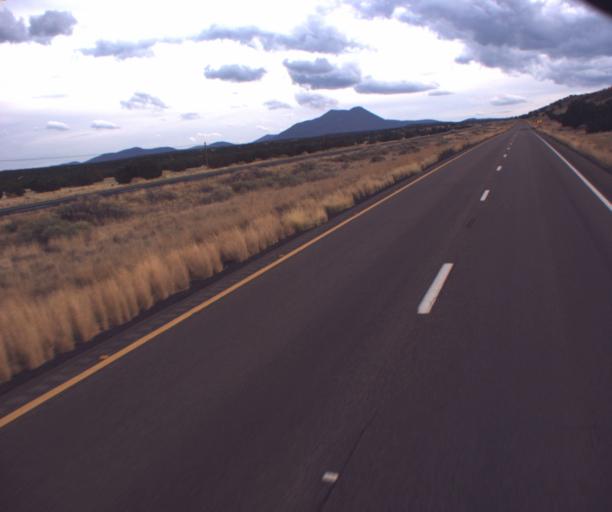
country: US
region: Arizona
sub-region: Coconino County
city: Flagstaff
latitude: 35.5281
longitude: -111.5422
